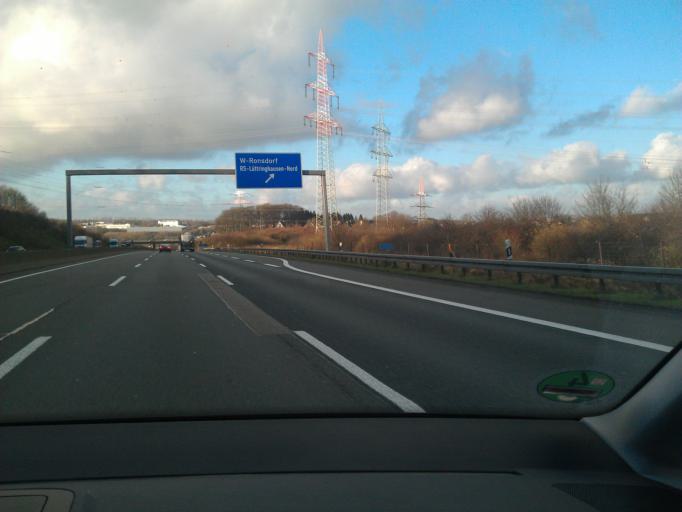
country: DE
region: North Rhine-Westphalia
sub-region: Regierungsbezirk Dusseldorf
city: Remscheid
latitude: 51.2245
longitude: 7.2399
